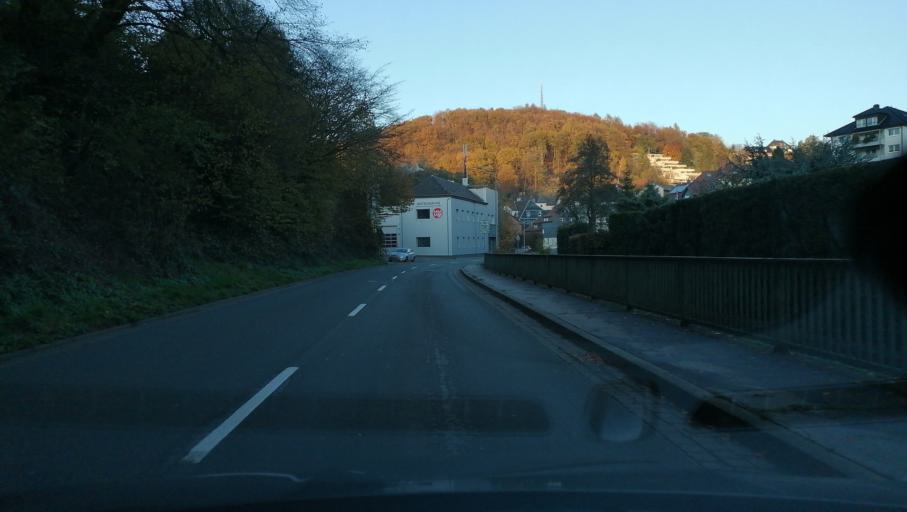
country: DE
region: North Rhine-Westphalia
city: Ennepetal
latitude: 51.2903
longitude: 7.3405
